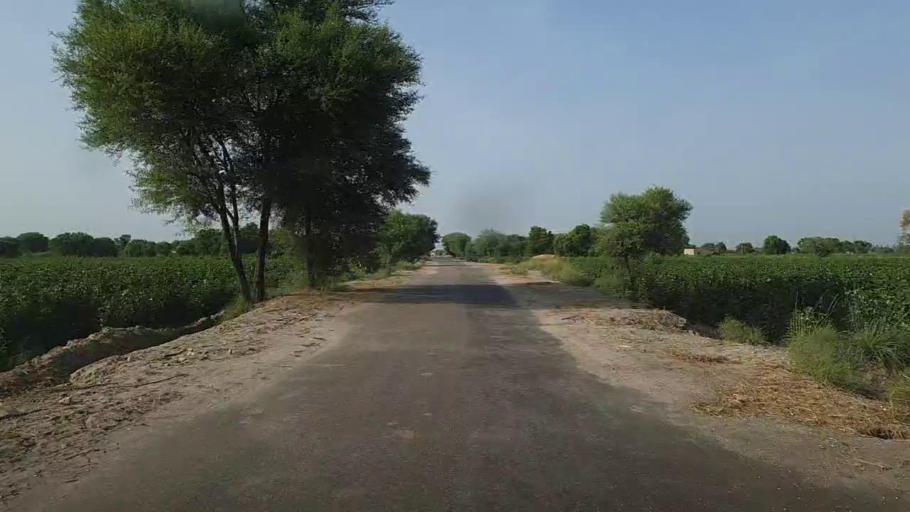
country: PK
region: Sindh
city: Ubauro
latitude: 28.0898
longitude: 69.8441
